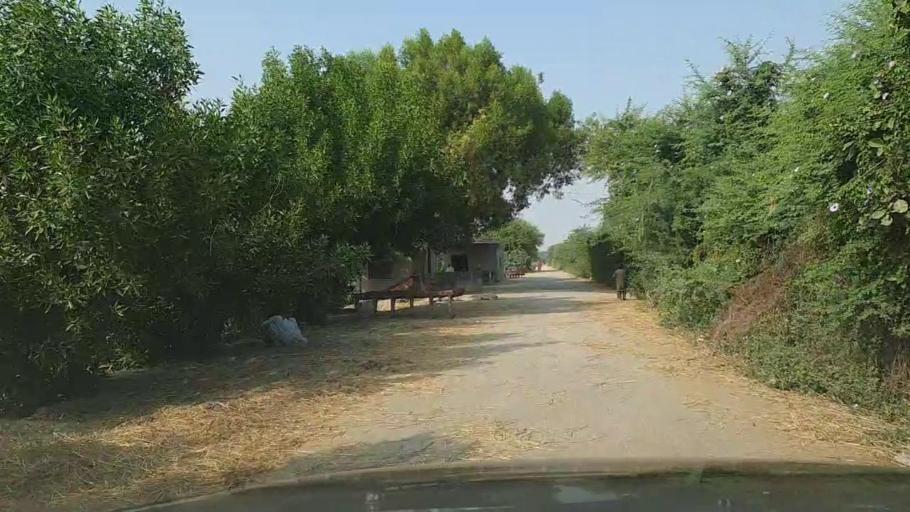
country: PK
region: Sindh
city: Mirpur Batoro
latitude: 24.7055
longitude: 68.2545
